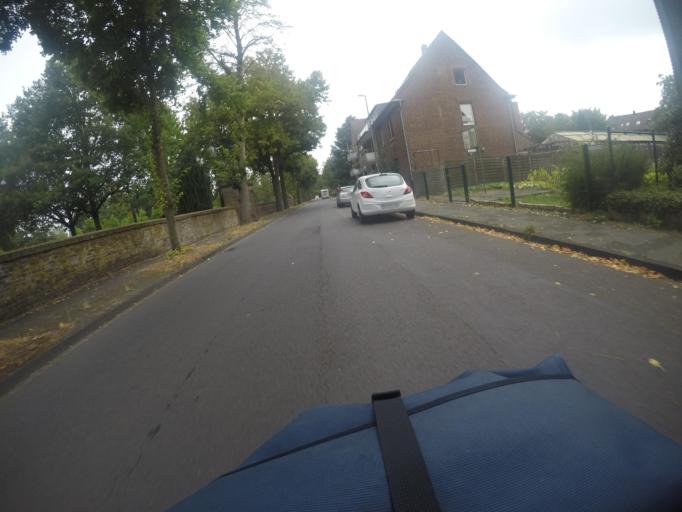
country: DE
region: North Rhine-Westphalia
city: Tonisvorst
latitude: 51.3797
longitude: 6.5054
